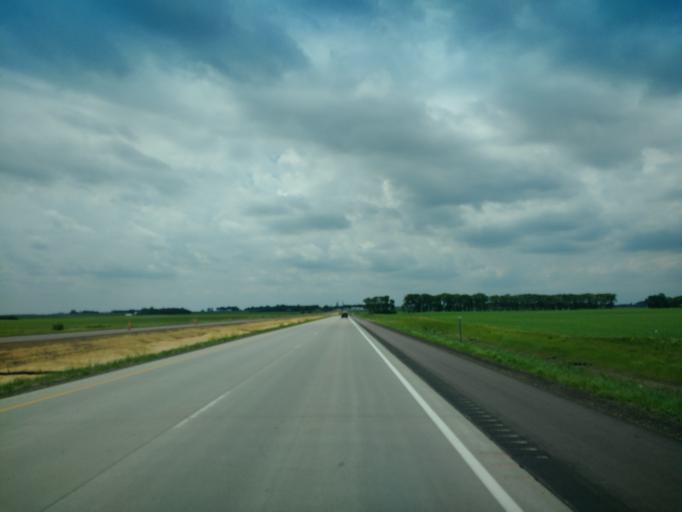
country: US
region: Minnesota
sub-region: Cottonwood County
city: Mountain Lake
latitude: 43.9159
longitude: -95.0103
